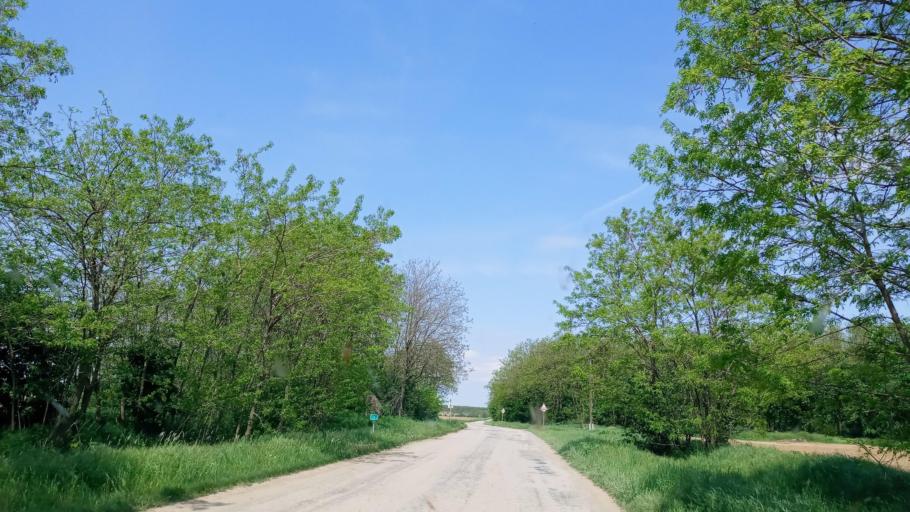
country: HU
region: Baranya
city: Boly
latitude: 45.8810
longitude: 18.5731
